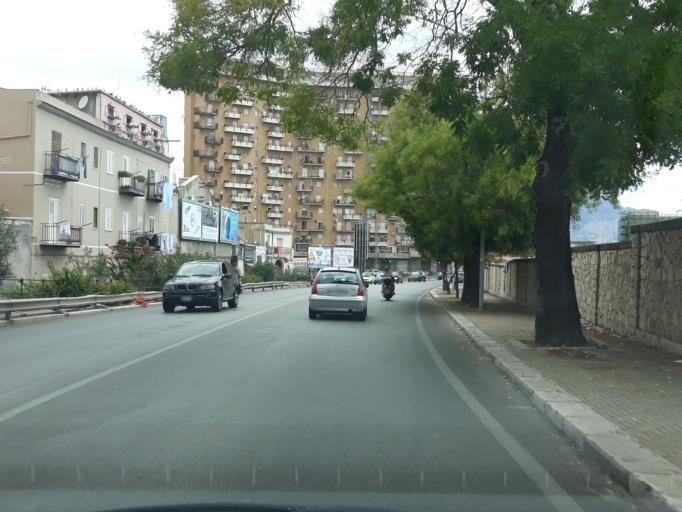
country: IT
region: Sicily
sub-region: Palermo
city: Ciaculli
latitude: 38.1100
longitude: 13.3791
